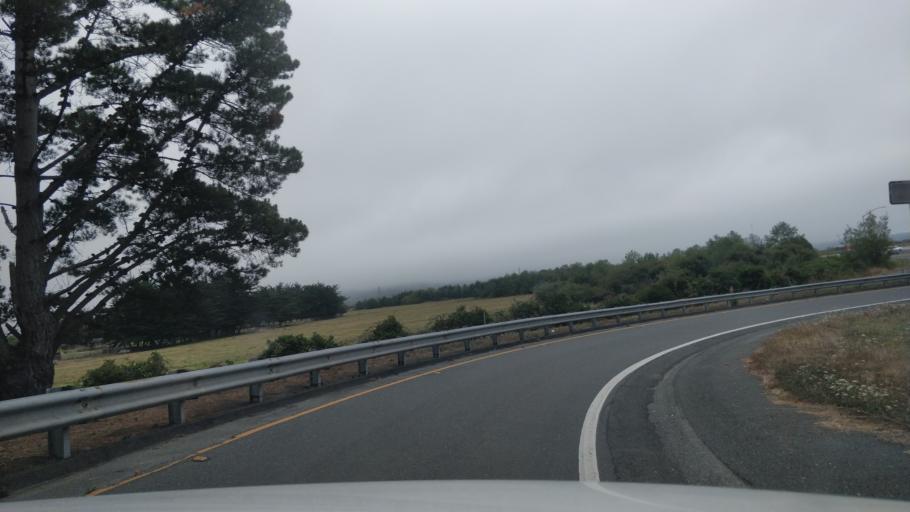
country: US
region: California
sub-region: Humboldt County
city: Arcata
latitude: 40.8622
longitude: -124.0813
